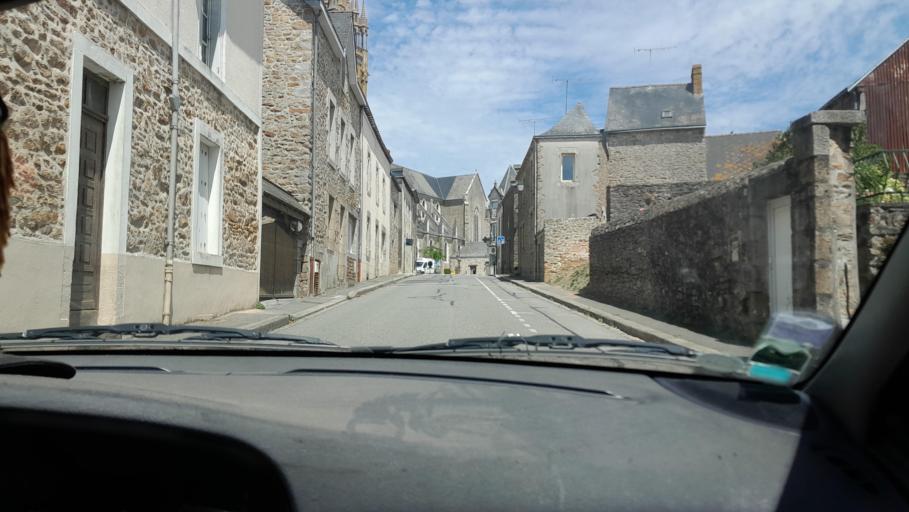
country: FR
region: Brittany
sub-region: Departement d'Ille-et-Vilaine
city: Le Pertre
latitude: 48.0334
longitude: -1.0362
